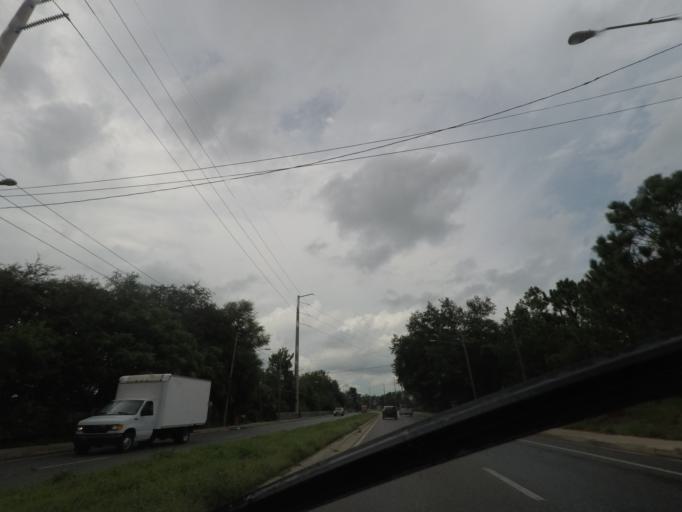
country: US
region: Florida
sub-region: Polk County
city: Loughman
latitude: 28.2388
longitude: -81.5616
